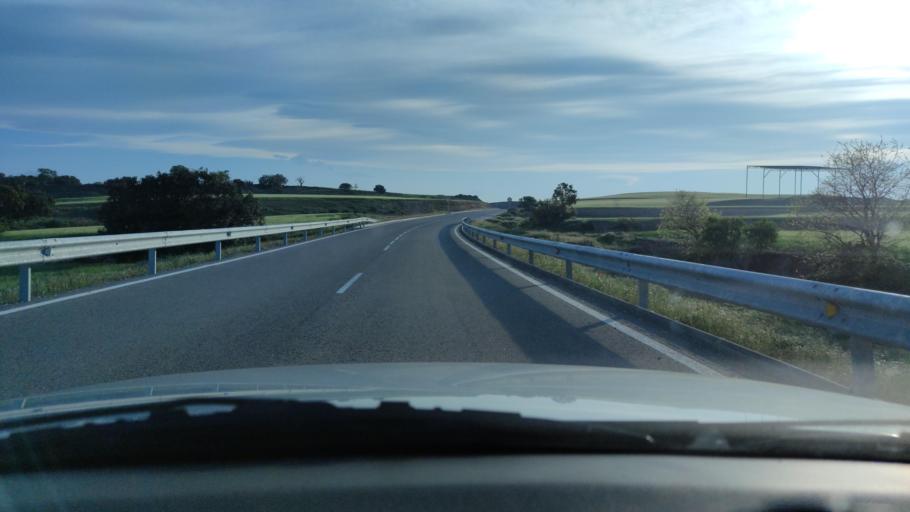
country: ES
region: Catalonia
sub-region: Provincia de Lleida
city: Castellsera
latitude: 41.7775
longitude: 1.0378
